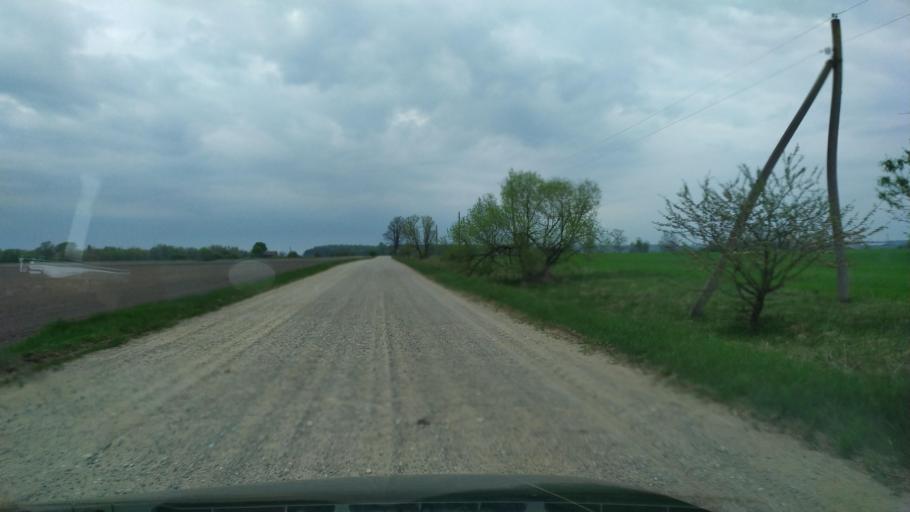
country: BY
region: Brest
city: Zhabinka
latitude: 52.1319
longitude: 24.0920
